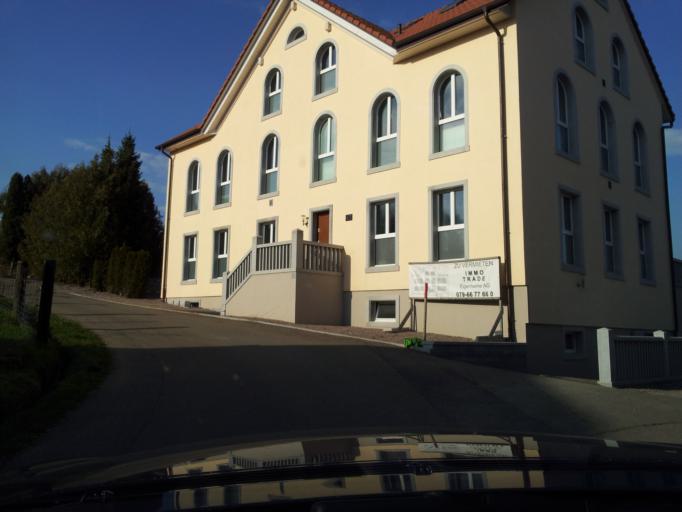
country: CH
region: Aargau
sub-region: Bezirk Bremgarten
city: Rudolfstetten
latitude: 47.3813
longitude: 8.3800
